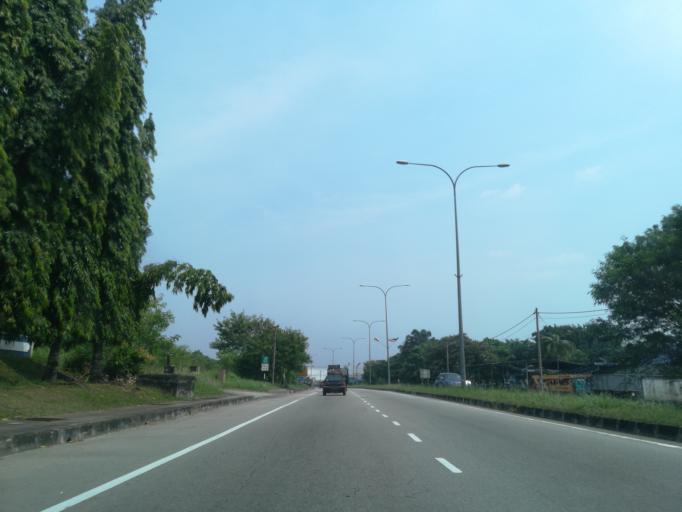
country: MY
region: Kedah
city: Kulim
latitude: 5.4063
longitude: 100.5521
